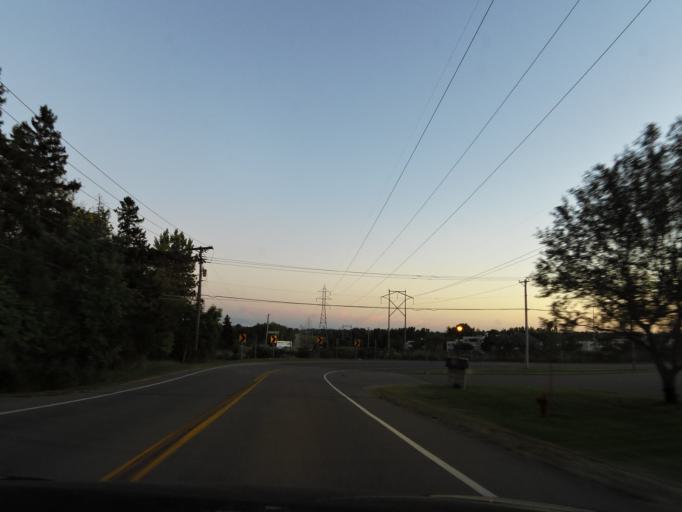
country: US
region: Minnesota
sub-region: Washington County
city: Oakdale
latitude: 44.9497
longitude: -92.9645
